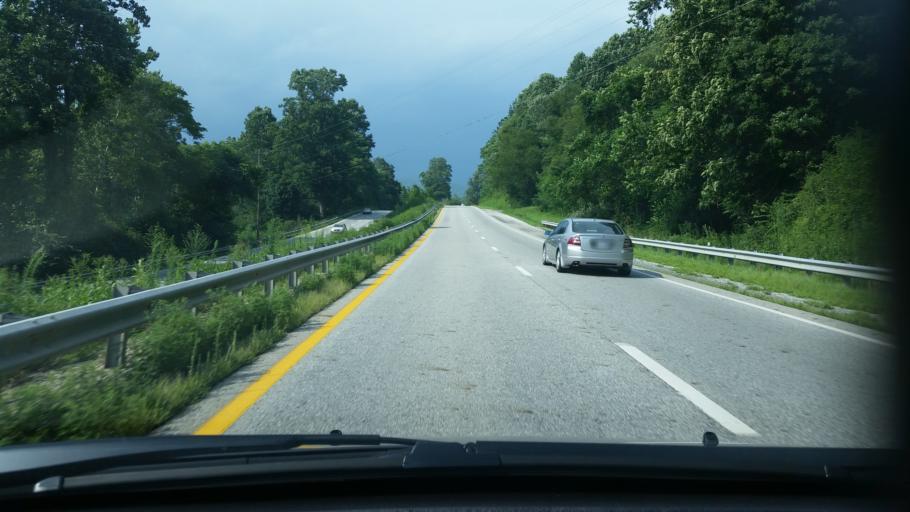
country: US
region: Virginia
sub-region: Nelson County
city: Lovingston
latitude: 37.7892
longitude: -78.8656
